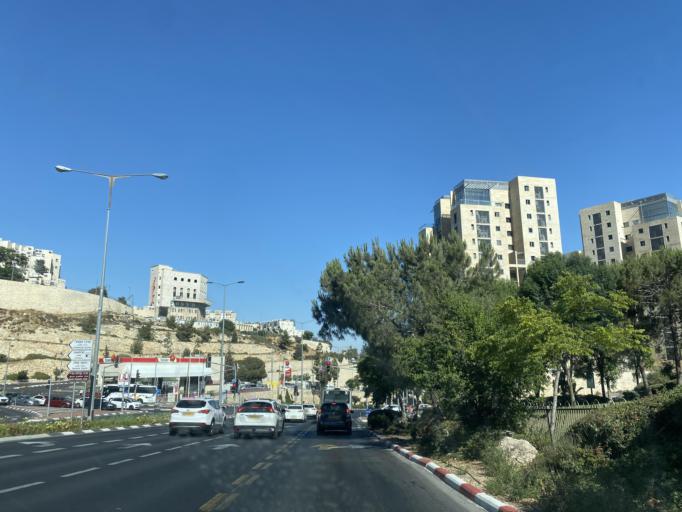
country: PS
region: West Bank
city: Bayt Iksa
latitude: 31.8191
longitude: 35.1931
